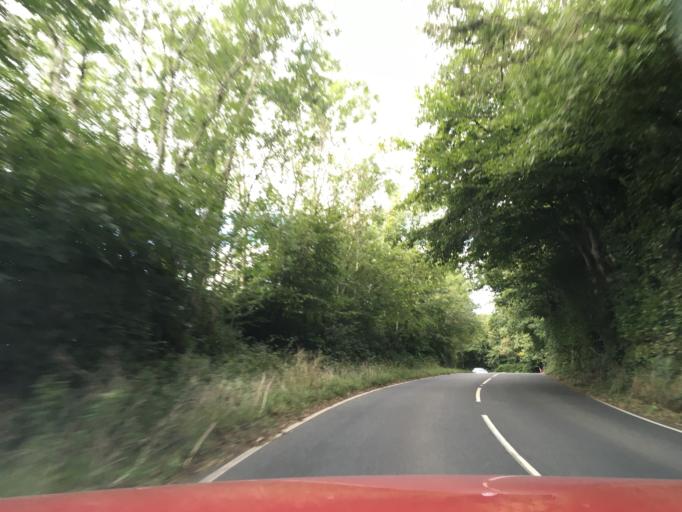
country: GB
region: England
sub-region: Devon
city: Honiton
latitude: 50.7481
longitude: -3.2088
